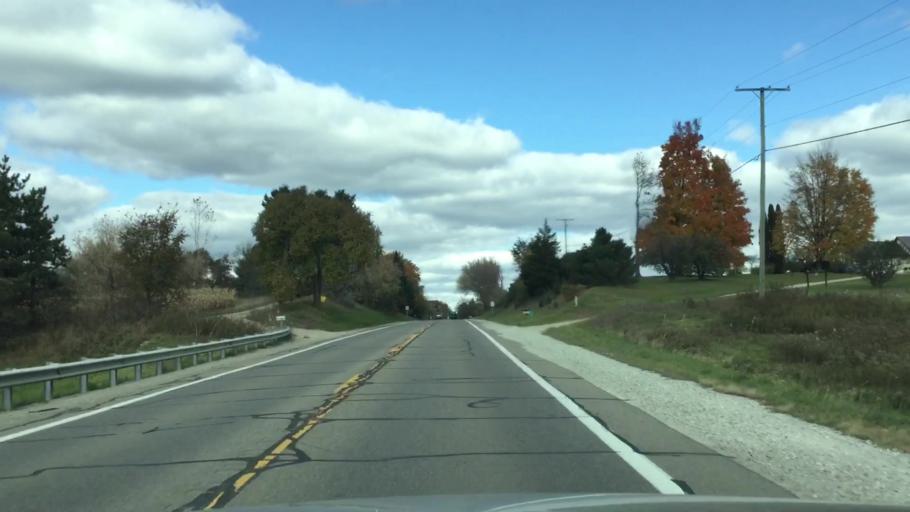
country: US
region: Michigan
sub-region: Lapeer County
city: Lapeer
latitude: 43.0987
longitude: -83.3081
